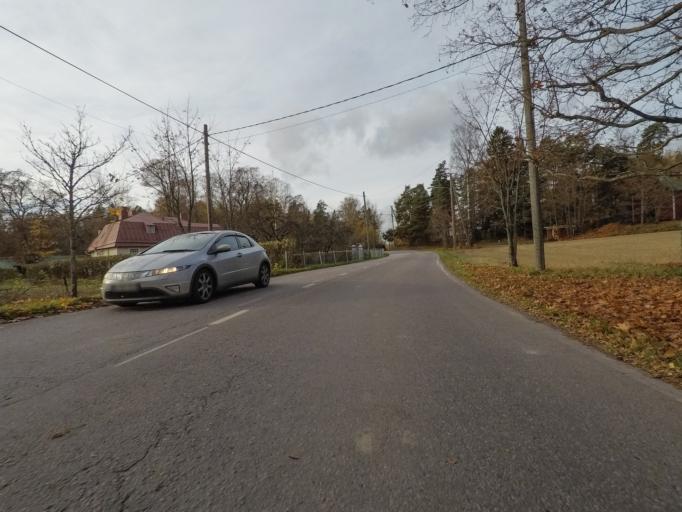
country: FI
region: Uusimaa
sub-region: Helsinki
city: Vantaa
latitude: 60.2565
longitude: 25.1415
